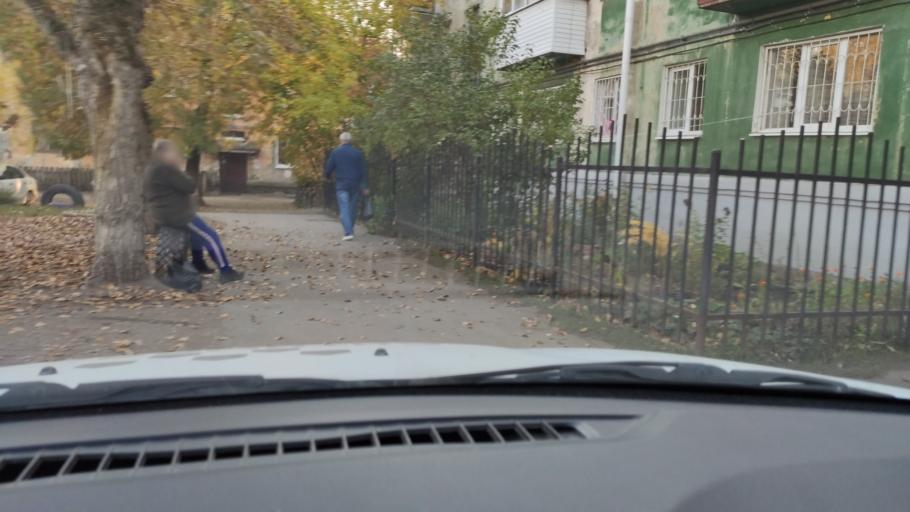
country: RU
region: Perm
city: Kondratovo
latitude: 57.9943
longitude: 56.1488
